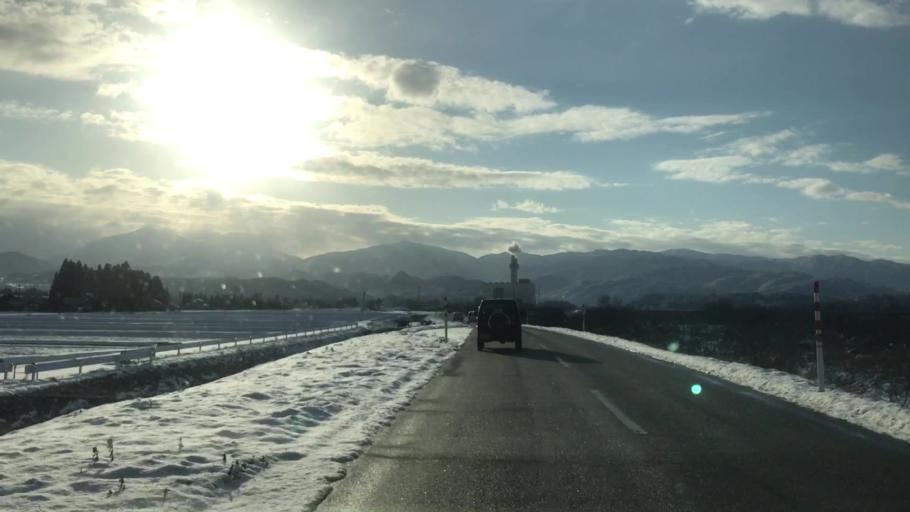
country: JP
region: Toyama
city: Kamiichi
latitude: 36.6333
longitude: 137.2946
